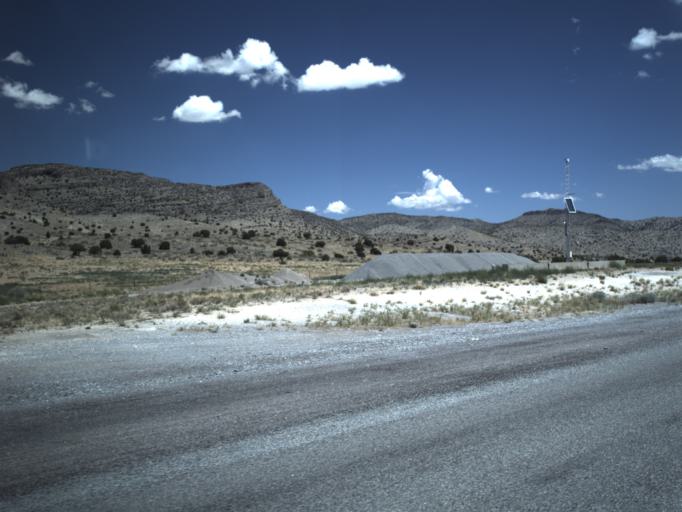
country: US
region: Utah
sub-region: Beaver County
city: Milford
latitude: 39.0739
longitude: -113.6397
